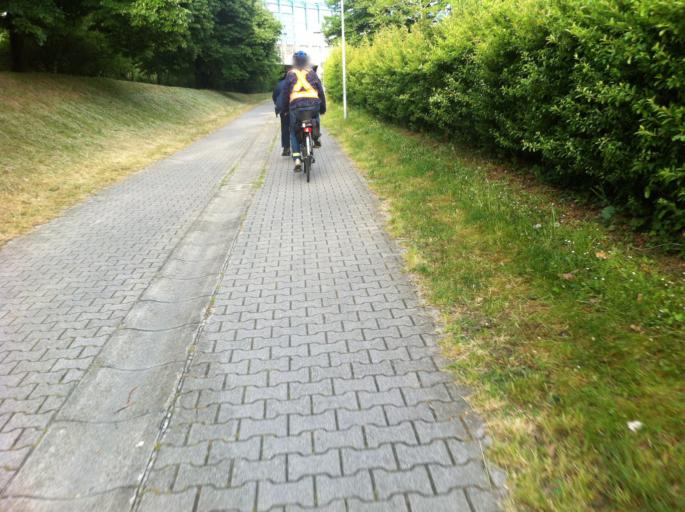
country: IT
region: Emilia-Romagna
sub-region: Provincia di Bologna
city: San Lazzaro
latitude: 44.4883
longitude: 11.3876
